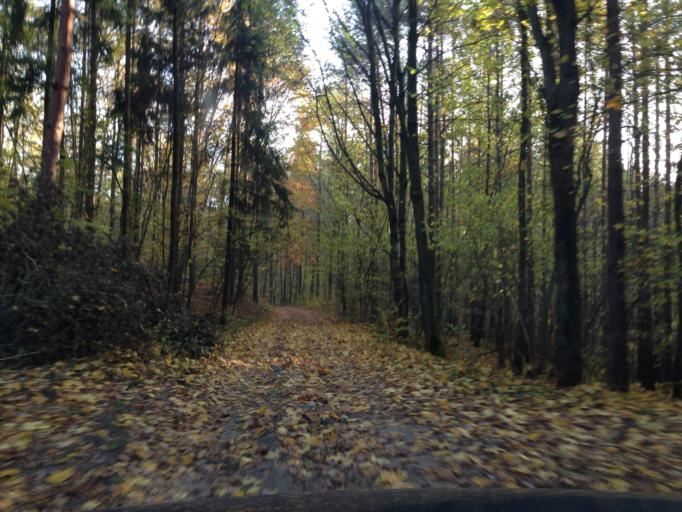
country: PL
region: Kujawsko-Pomorskie
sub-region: Powiat brodnicki
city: Gorzno
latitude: 53.2623
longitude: 19.7177
